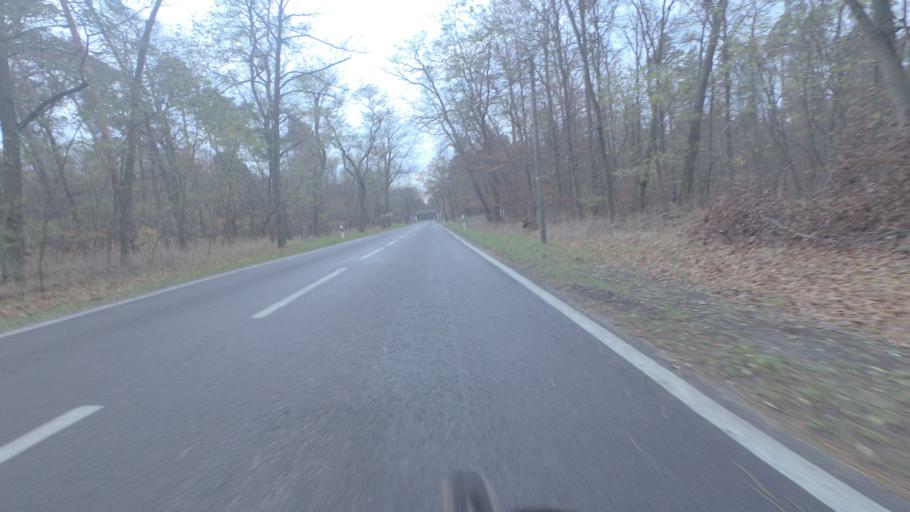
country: DE
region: Brandenburg
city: Michendorf
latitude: 52.3052
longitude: 13.1185
